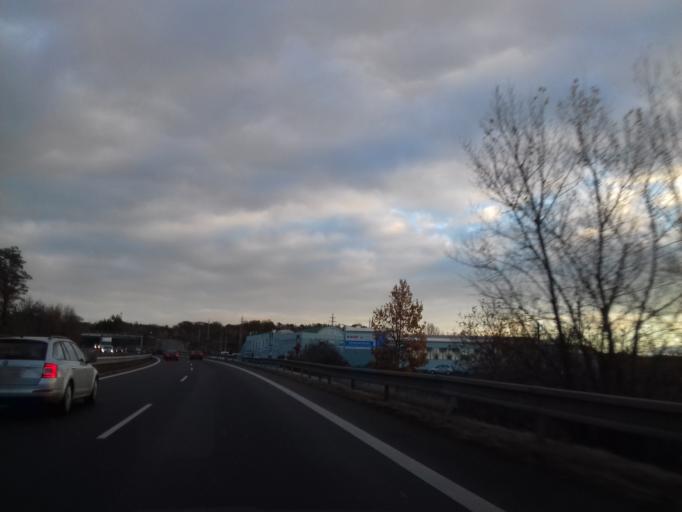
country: CZ
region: Olomoucky
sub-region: Okres Prostejov
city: Prostejov
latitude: 49.4875
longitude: 17.1386
